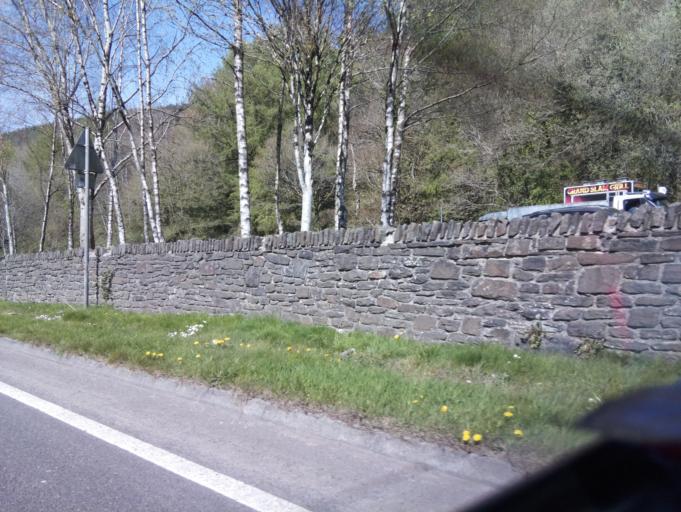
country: GB
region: Wales
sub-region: Rhondda Cynon Taf
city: Mountain Ash
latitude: 51.6690
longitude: -3.3569
